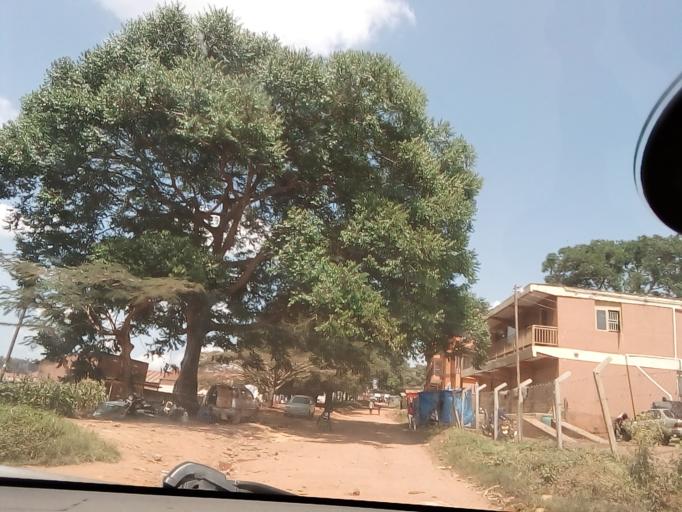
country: UG
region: Central Region
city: Masaka
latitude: -0.3386
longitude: 31.7409
